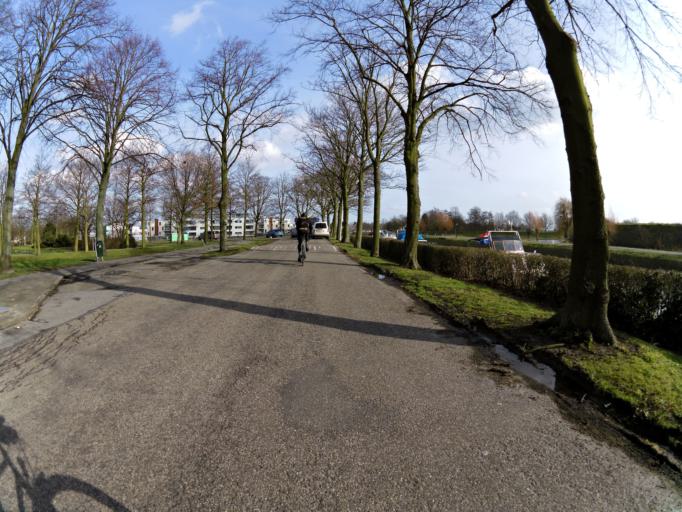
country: NL
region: South Holland
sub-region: Gemeente Brielle
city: Brielle
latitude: 51.9073
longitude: 4.1694
